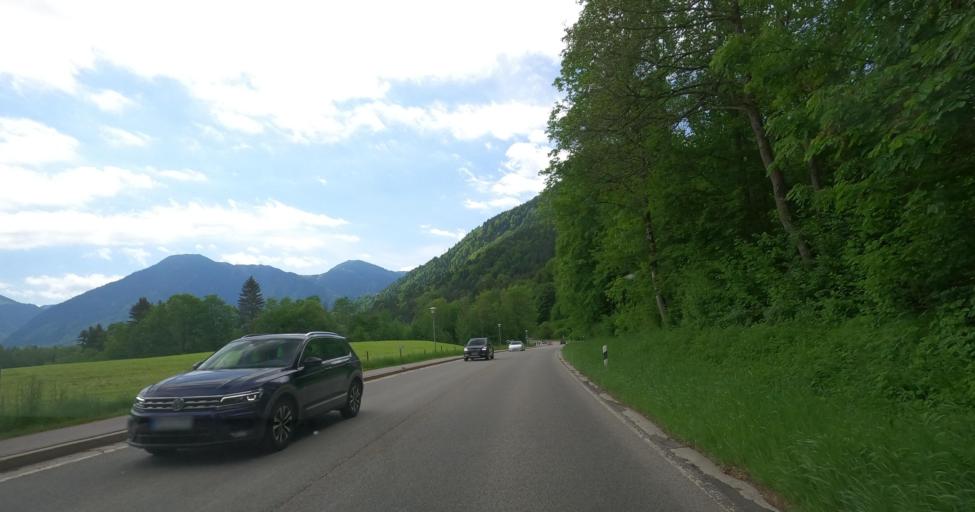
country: DE
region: Bavaria
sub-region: Upper Bavaria
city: Bad Wiessee
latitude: 47.6977
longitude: 11.7316
